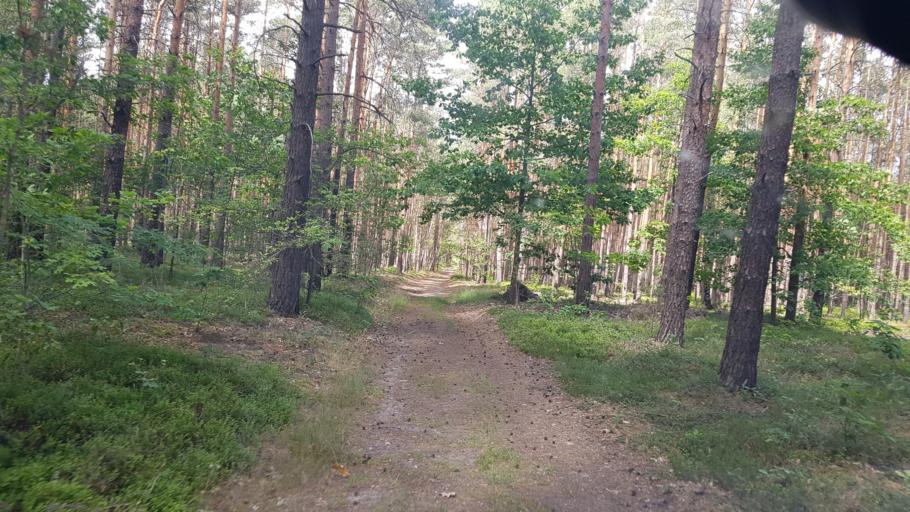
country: DE
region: Brandenburg
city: Sallgast
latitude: 51.6015
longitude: 13.8360
